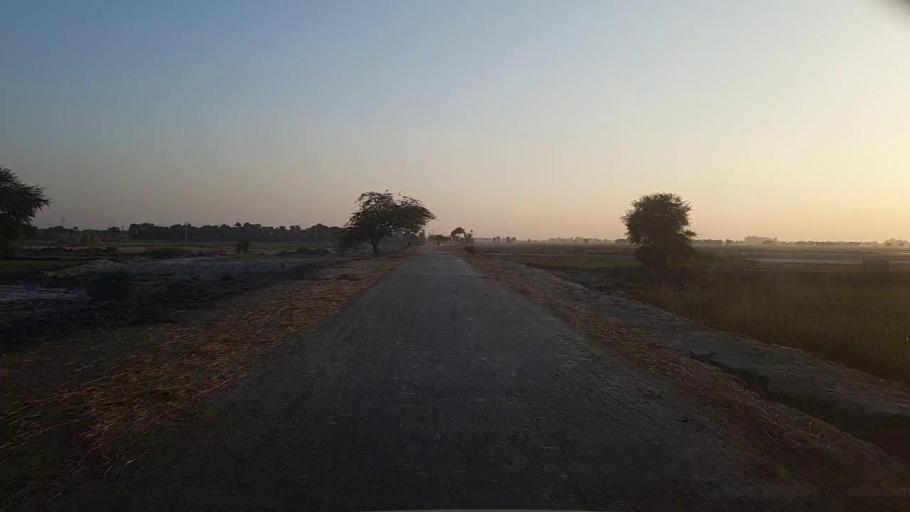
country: PK
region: Sindh
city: Khairpur Nathan Shah
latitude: 27.1747
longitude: 67.7338
